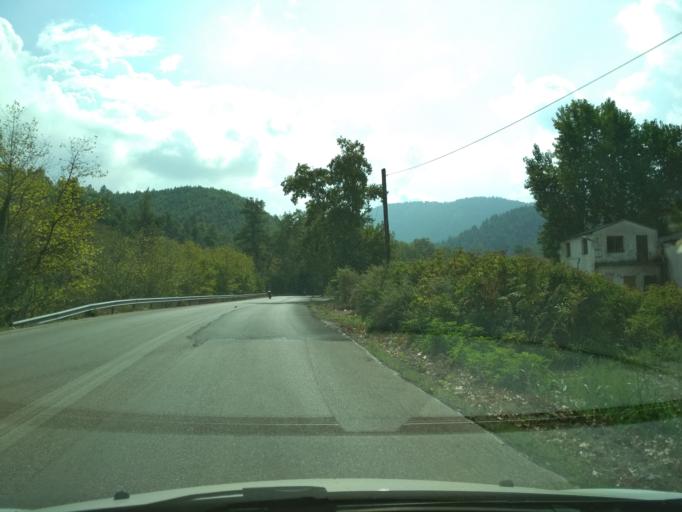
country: GR
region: Central Greece
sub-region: Nomos Evvoias
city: Prokopion
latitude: 38.7210
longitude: 23.5141
